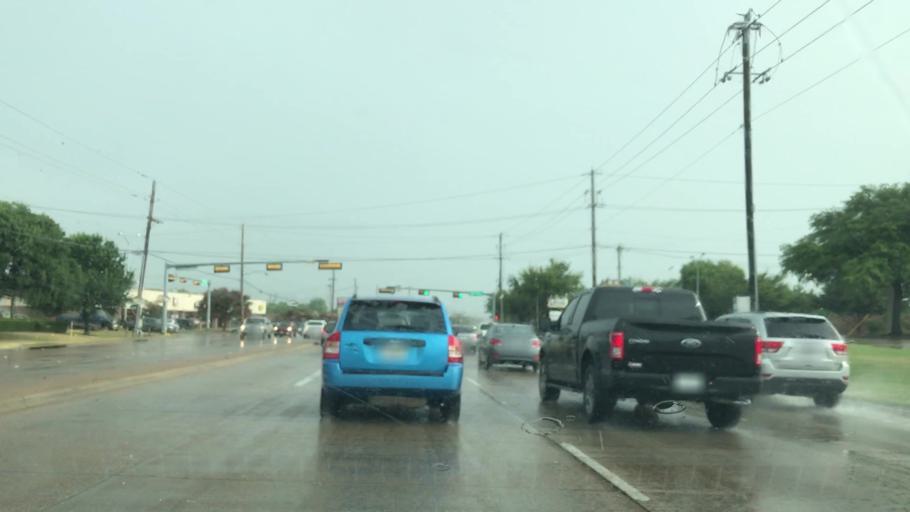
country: US
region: Texas
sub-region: Dallas County
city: Richardson
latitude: 32.8953
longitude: -96.7006
